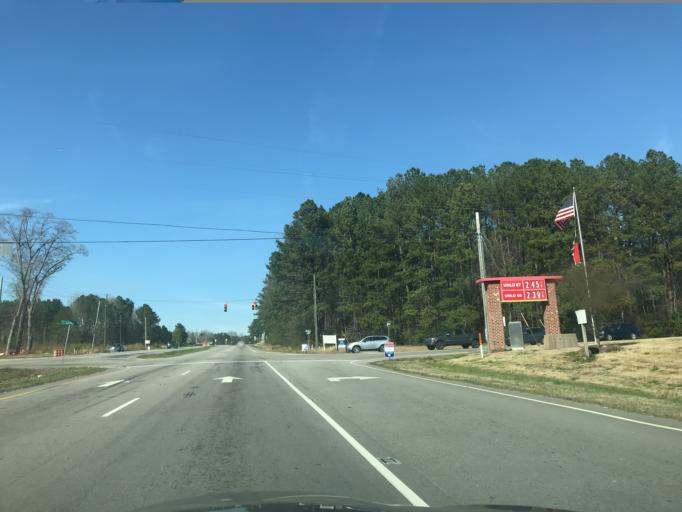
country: US
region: North Carolina
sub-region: Wake County
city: Fuquay-Varina
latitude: 35.6351
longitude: -78.7145
